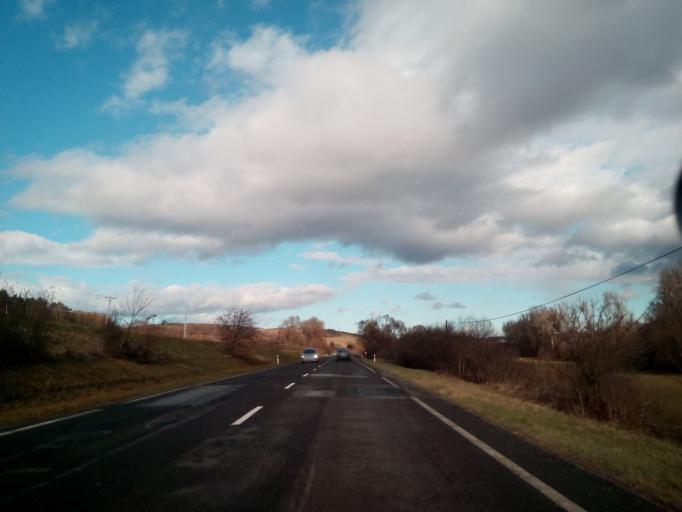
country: SK
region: Presovsky
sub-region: Okres Bardejov
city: Bardejov
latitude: 49.1657
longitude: 21.3114
